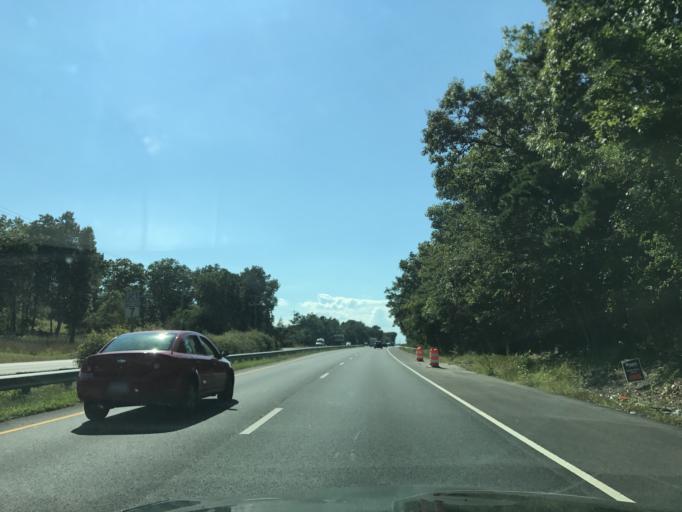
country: US
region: Maryland
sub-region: Cecil County
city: Charlestown
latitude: 39.5854
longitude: -76.0102
